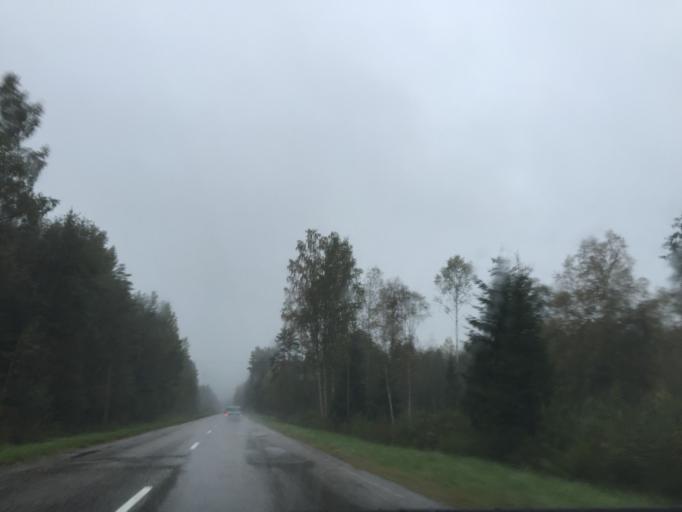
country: LV
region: Ropazu
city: Ropazi
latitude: 56.9904
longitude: 24.6400
